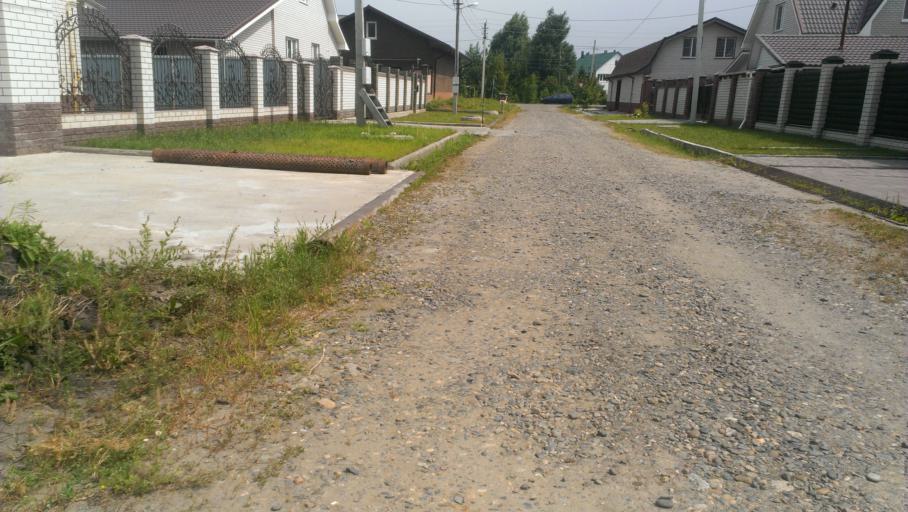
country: RU
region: Altai Krai
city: Novosilikatnyy
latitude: 53.3705
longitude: 83.6500
